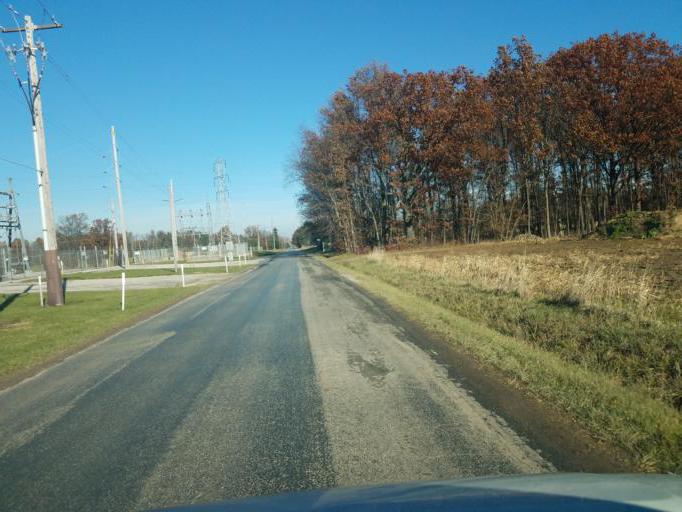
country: US
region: Ohio
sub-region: Ashland County
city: Ashland
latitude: 40.8210
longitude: -82.3494
